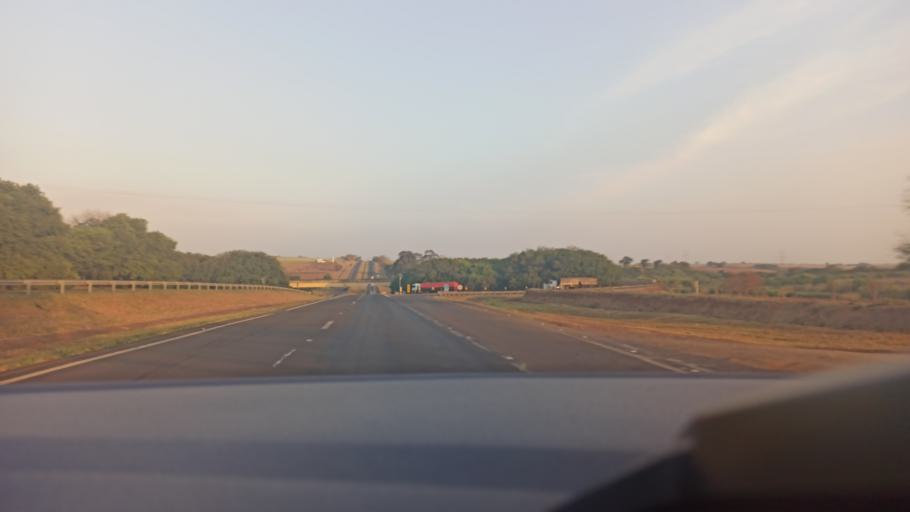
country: BR
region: Sao Paulo
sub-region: Santa Adelia
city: Santa Adelia
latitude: -21.3696
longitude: -48.7515
